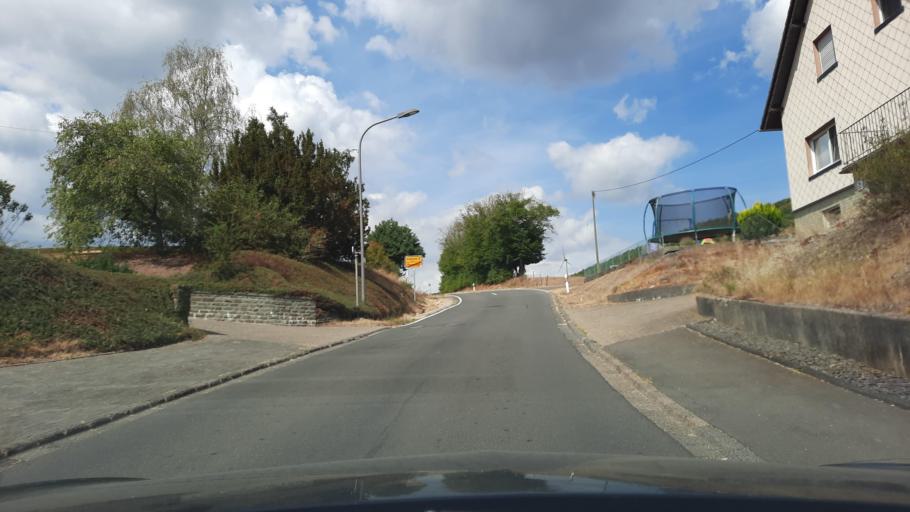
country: DE
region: Rheinland-Pfalz
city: Pronsfeld
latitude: 50.1617
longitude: 6.3304
